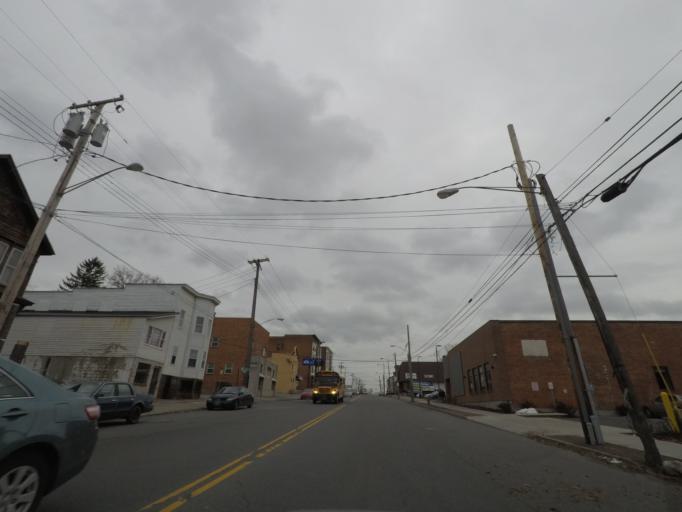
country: US
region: New York
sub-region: Schenectady County
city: Schenectady
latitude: 42.8095
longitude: -73.9371
